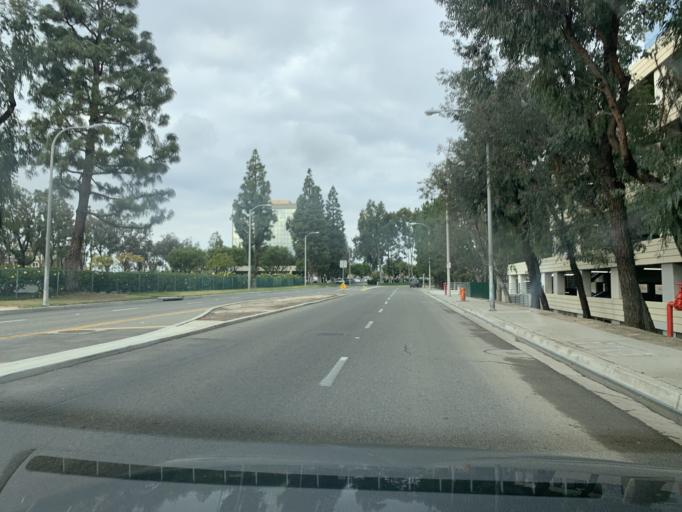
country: US
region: California
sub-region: Orange County
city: Orange
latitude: 33.7862
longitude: -117.8944
